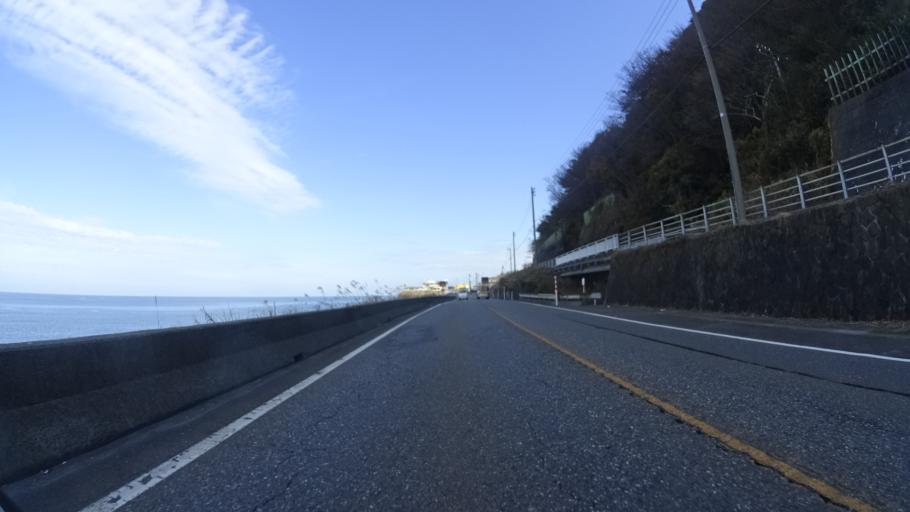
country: JP
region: Niigata
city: Itoigawa
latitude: 37.0817
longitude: 137.9441
